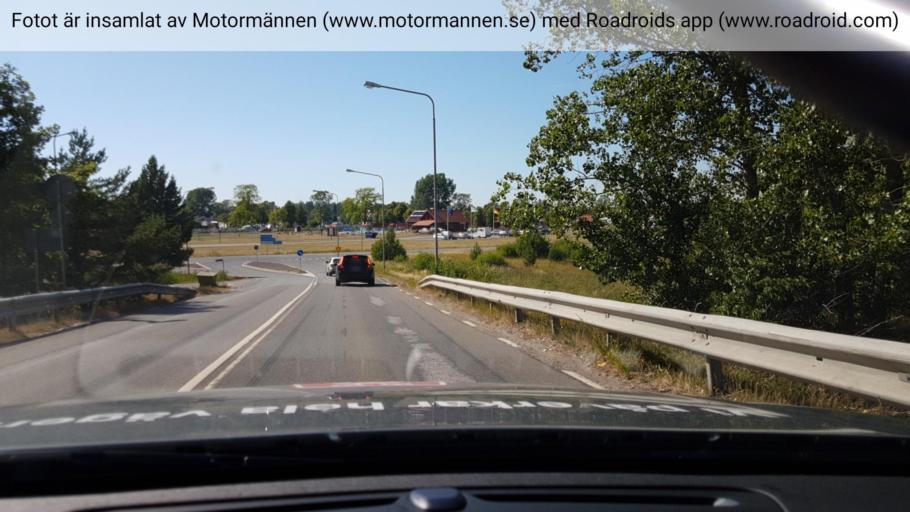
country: SE
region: Vaestra Goetaland
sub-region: Toreboda Kommun
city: Toereboda
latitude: 58.7123
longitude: 14.1333
